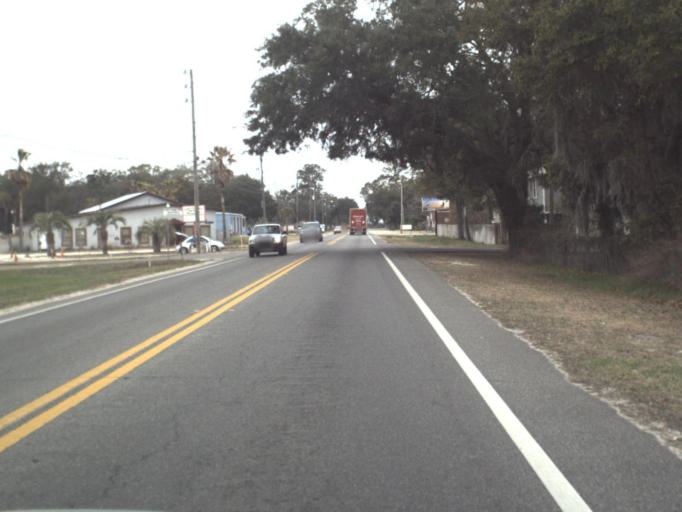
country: US
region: Florida
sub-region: Bay County
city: Parker
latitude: 30.1311
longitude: -85.6072
